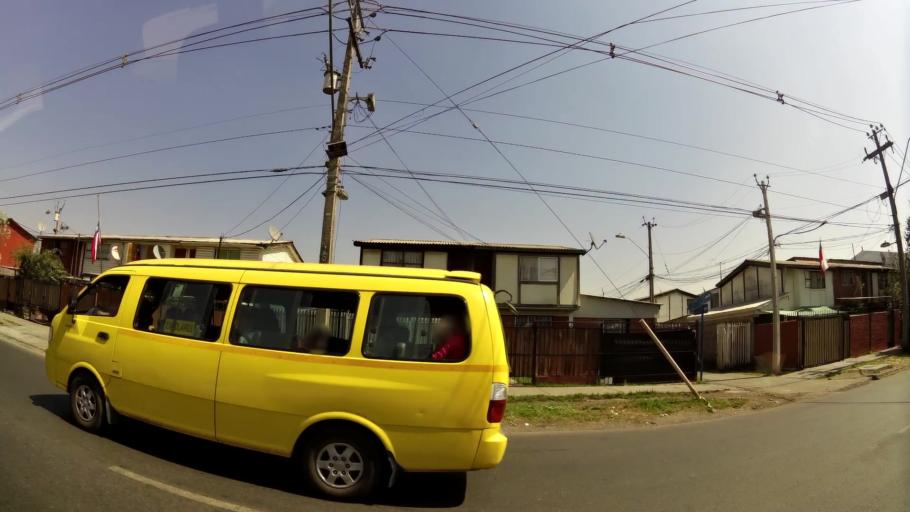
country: CL
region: Santiago Metropolitan
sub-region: Provincia de Santiago
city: La Pintana
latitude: -33.5524
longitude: -70.6132
